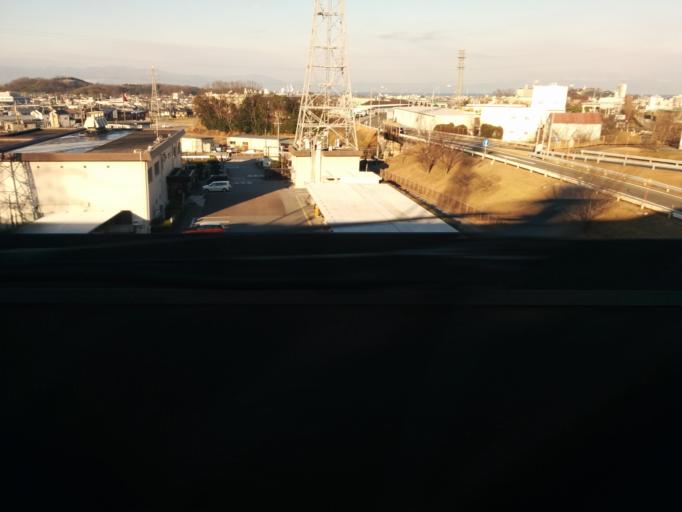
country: JP
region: Shiga Prefecture
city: Hikone
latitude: 35.2580
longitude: 136.2765
